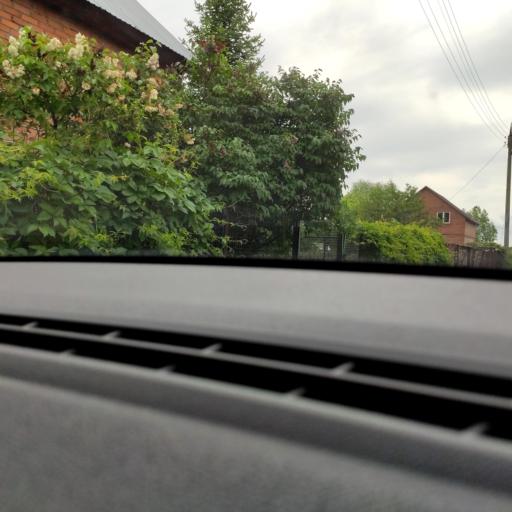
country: RU
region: Samara
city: Podstepki
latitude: 53.5029
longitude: 49.1609
